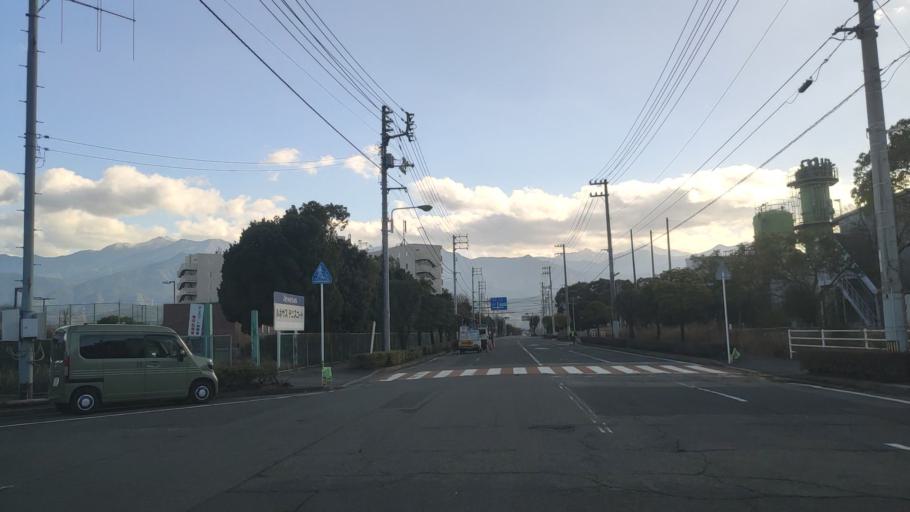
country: JP
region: Ehime
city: Saijo
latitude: 33.9370
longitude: 133.1921
